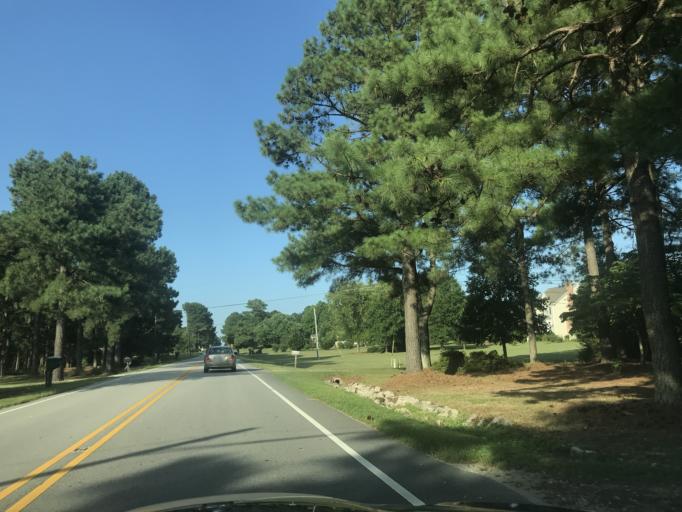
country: US
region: North Carolina
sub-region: Wake County
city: Rolesville
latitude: 35.9307
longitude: -78.4455
